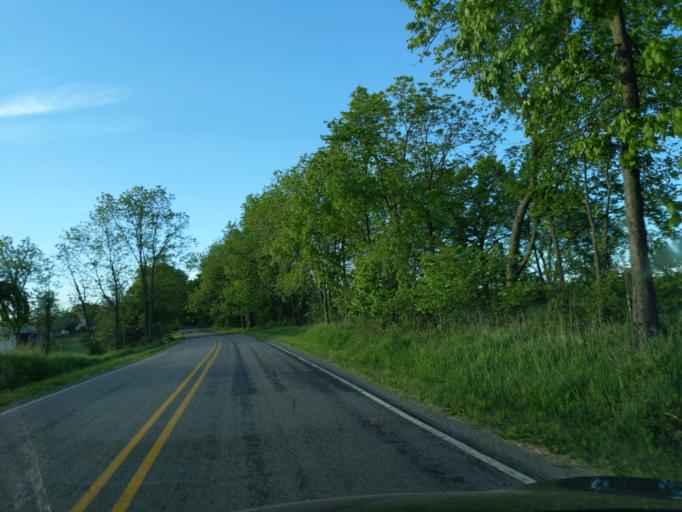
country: US
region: Michigan
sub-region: Ingham County
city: Leslie
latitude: 42.4458
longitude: -84.3132
